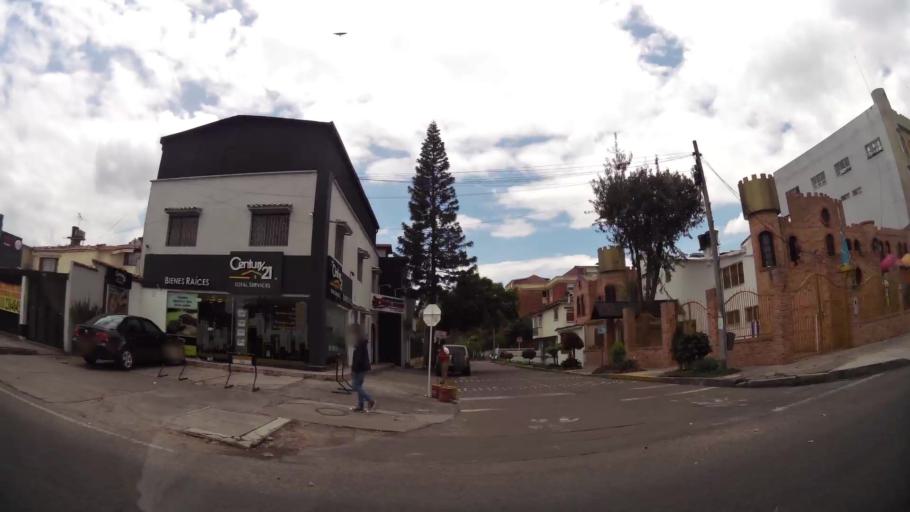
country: CO
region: Bogota D.C.
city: Barrio San Luis
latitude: 4.7214
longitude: -74.0673
